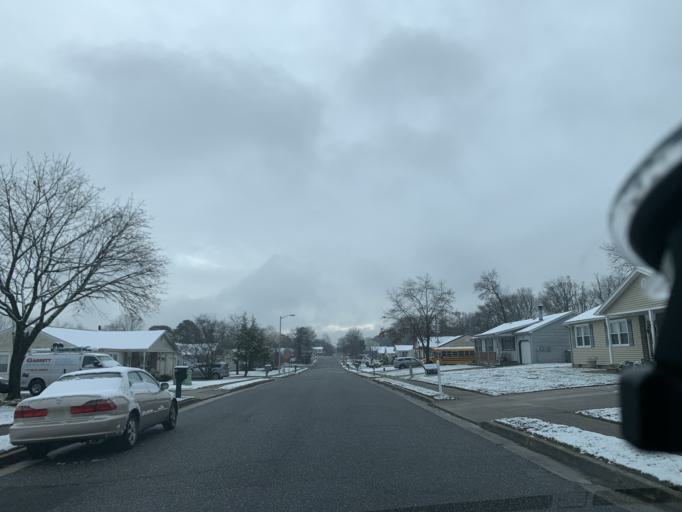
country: US
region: New Jersey
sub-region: Atlantic County
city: Pomona
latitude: 39.4332
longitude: -74.5938
